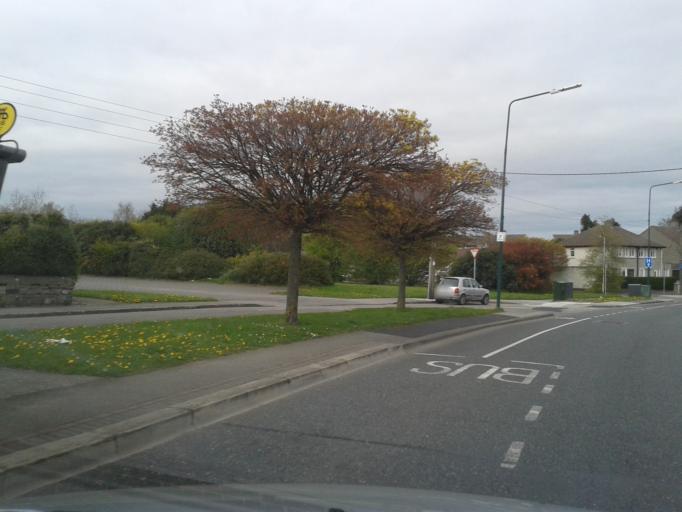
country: IE
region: Leinster
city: Beaumont
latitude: 53.3842
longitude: -6.2368
